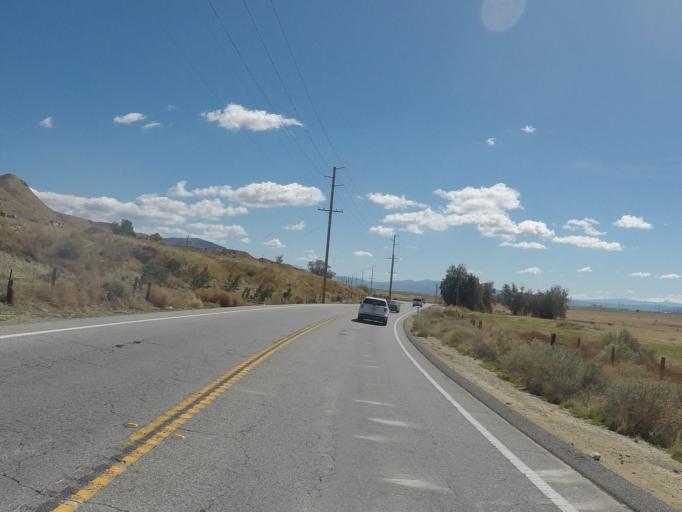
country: US
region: California
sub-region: Riverside County
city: Lakeview
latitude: 33.8807
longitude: -117.0579
